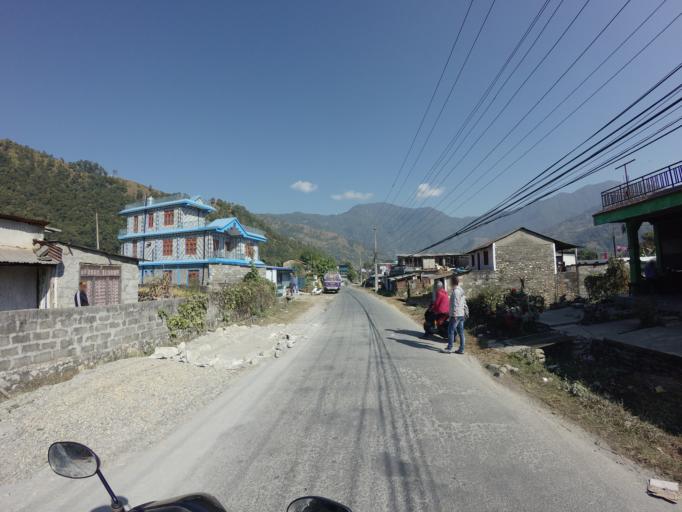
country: NP
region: Western Region
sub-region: Gandaki Zone
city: Pokhara
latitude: 28.2692
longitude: 83.9793
